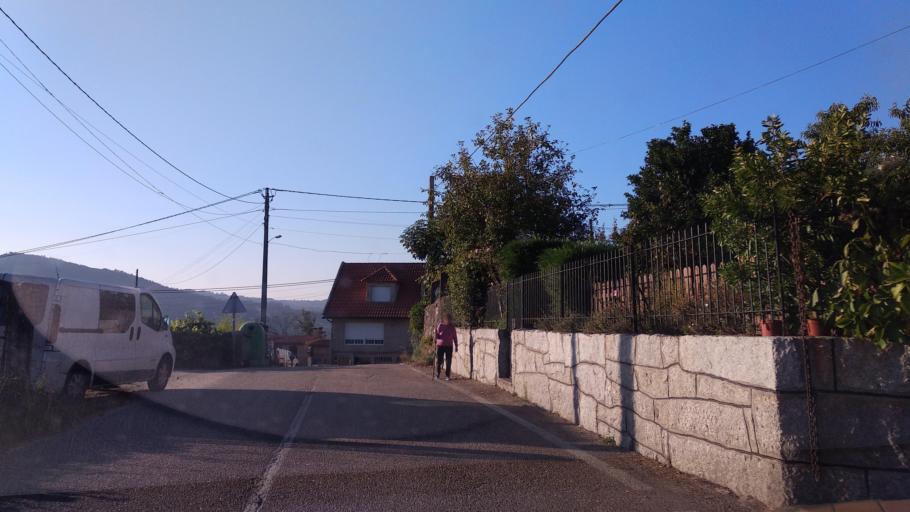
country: ES
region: Galicia
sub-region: Provincia de Pontevedra
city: Ponte Caldelas
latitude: 42.3632
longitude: -8.5319
